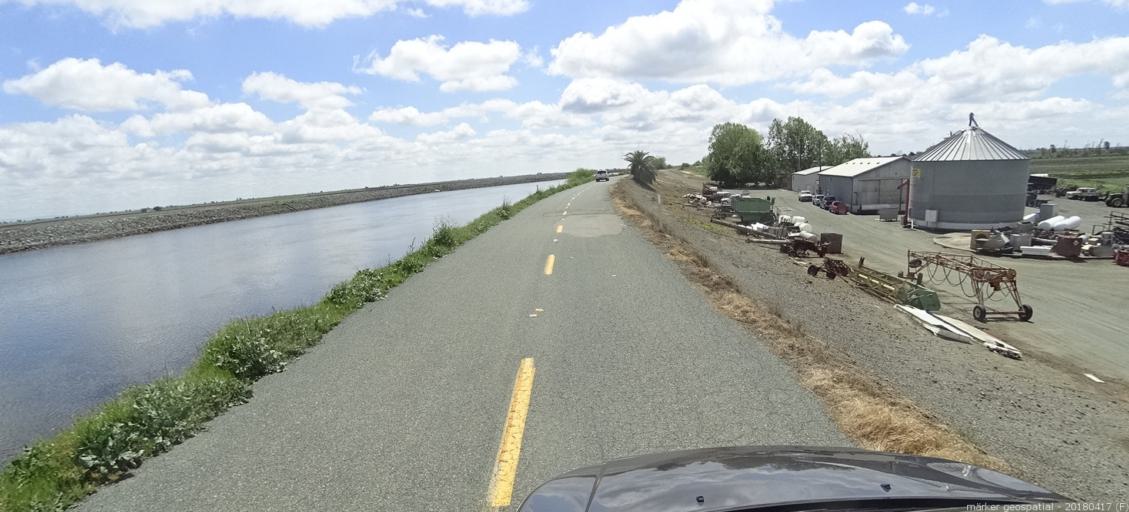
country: US
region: California
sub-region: Sacramento County
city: Walnut Grove
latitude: 38.1906
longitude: -121.5281
